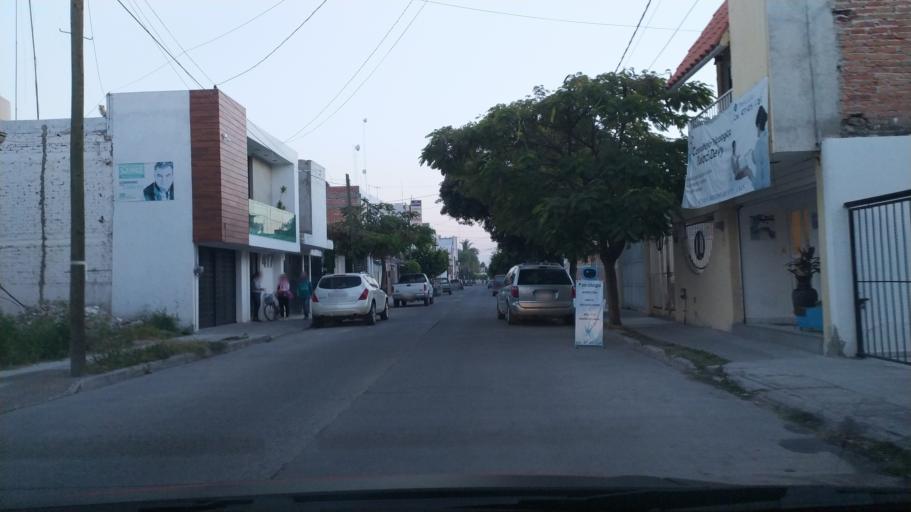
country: MX
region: Guanajuato
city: San Francisco del Rincon
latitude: 21.0126
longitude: -101.8613
